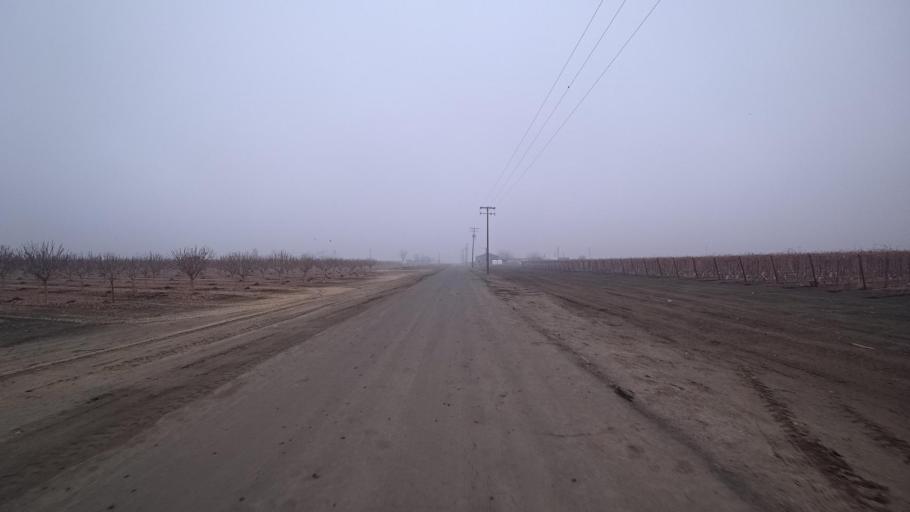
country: US
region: California
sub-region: Kern County
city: Buttonwillow
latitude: 35.4269
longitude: -119.5215
